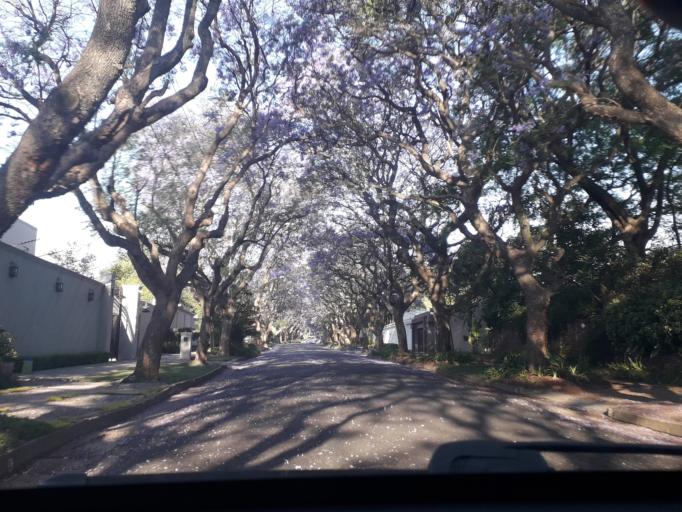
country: ZA
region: Gauteng
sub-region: City of Johannesburg Metropolitan Municipality
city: Johannesburg
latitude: -26.1525
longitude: 28.0406
